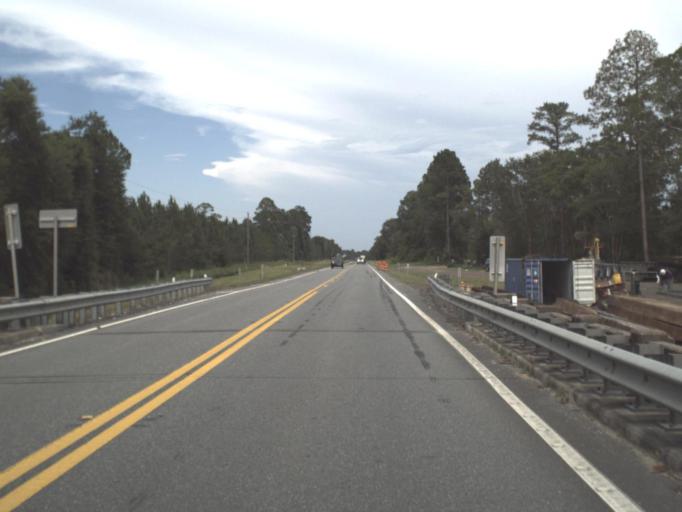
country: US
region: Florida
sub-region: Taylor County
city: Perry
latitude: 30.0982
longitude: -83.4718
